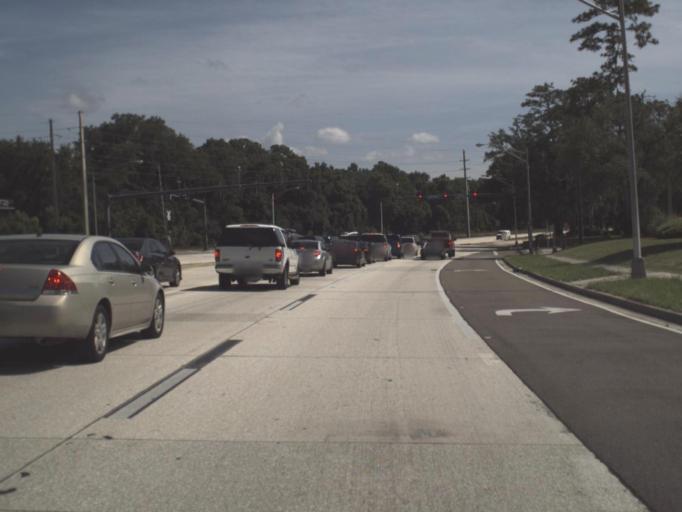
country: US
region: Florida
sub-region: Duval County
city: Jacksonville
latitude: 30.3018
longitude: -81.7200
